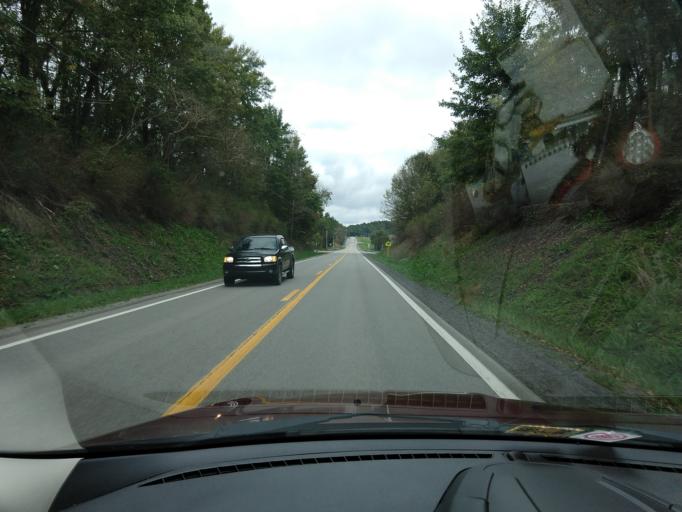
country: US
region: West Virginia
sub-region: Barbour County
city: Philippi
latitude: 39.1045
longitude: -79.9950
